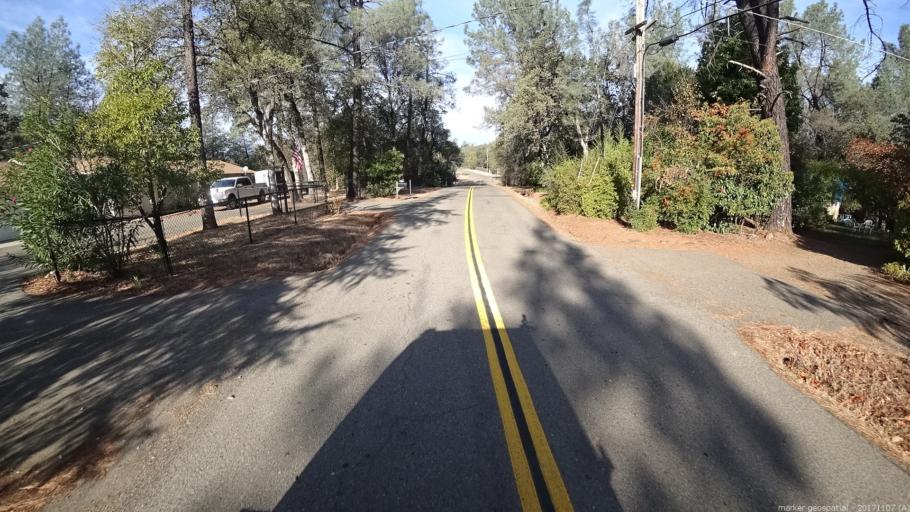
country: US
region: California
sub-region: Shasta County
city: Redding
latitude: 40.5500
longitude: -122.4405
